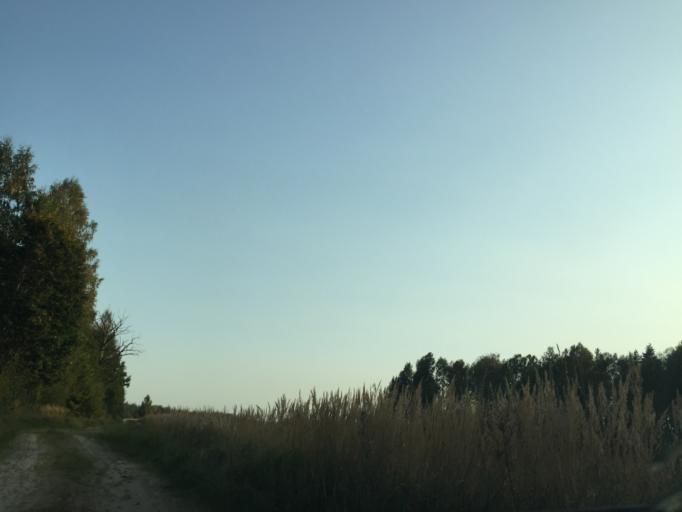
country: LV
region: Lielvarde
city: Lielvarde
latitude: 56.7874
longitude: 24.8361
